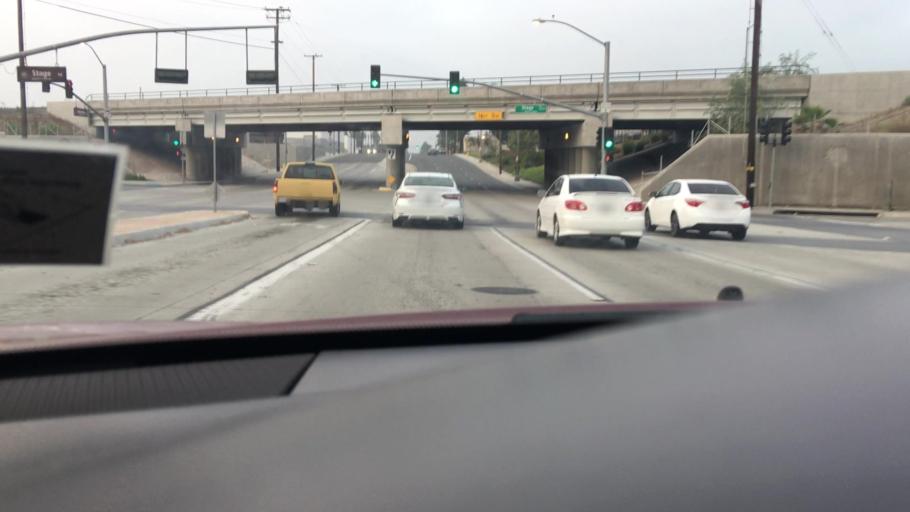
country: US
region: California
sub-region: Los Angeles County
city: La Mirada
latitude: 33.8982
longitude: -118.0292
